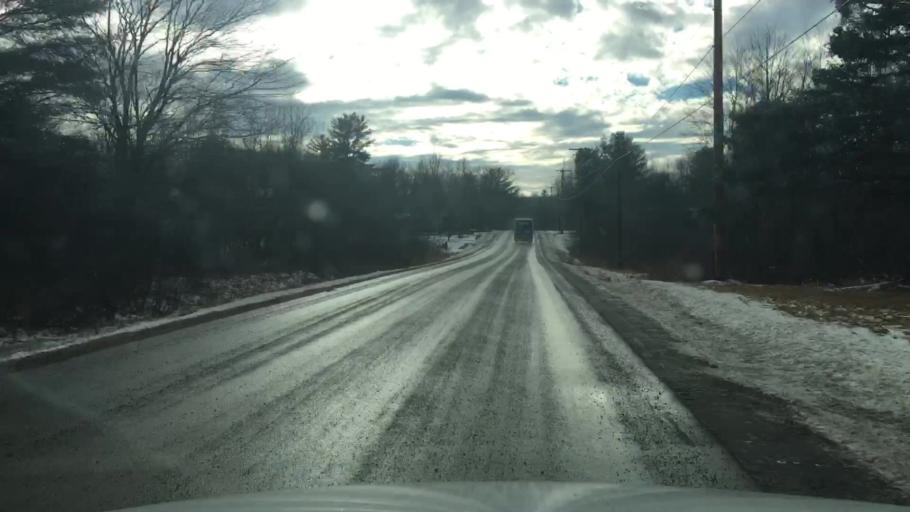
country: US
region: Maine
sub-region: Penobscot County
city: Brewer
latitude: 44.7267
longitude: -68.7559
